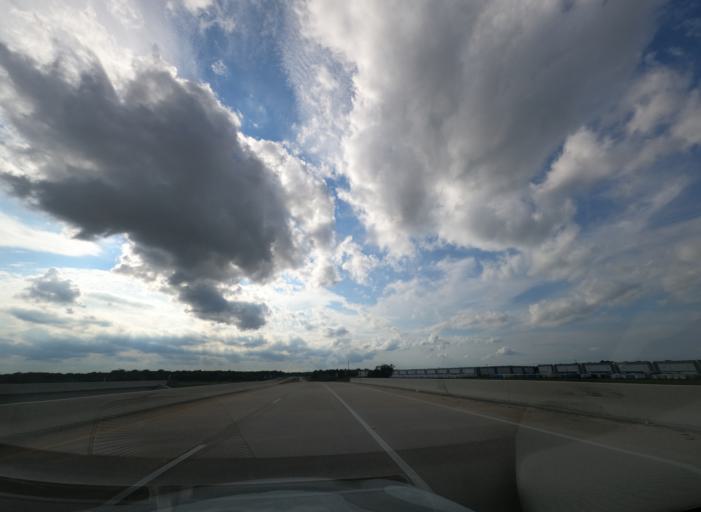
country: US
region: Tennessee
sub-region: Fayette County
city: Piperton
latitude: 34.9860
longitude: -89.5964
